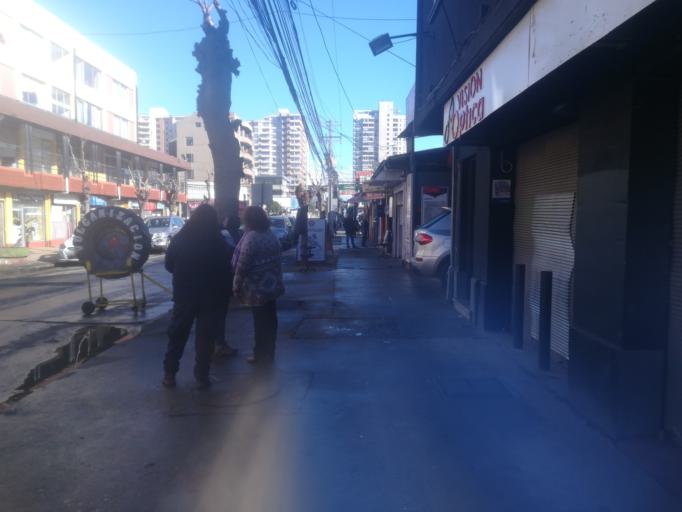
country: CL
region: Valparaiso
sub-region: Provincia de Valparaiso
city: Vina del Mar
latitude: -33.0101
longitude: -71.5419
